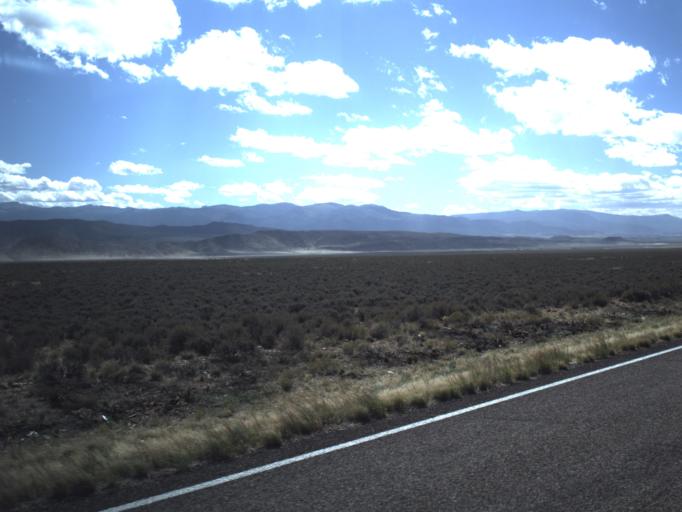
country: US
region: Utah
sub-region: Iron County
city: Enoch
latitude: 37.9510
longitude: -113.0151
